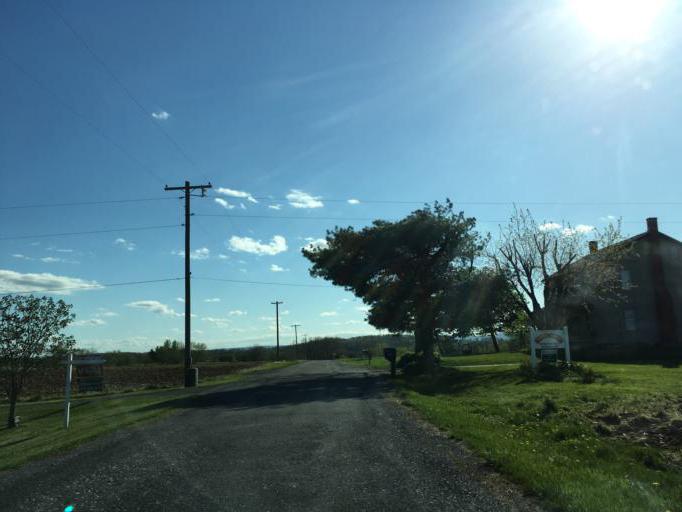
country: US
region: Maryland
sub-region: Frederick County
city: Emmitsburg
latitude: 39.6455
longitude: -77.2933
